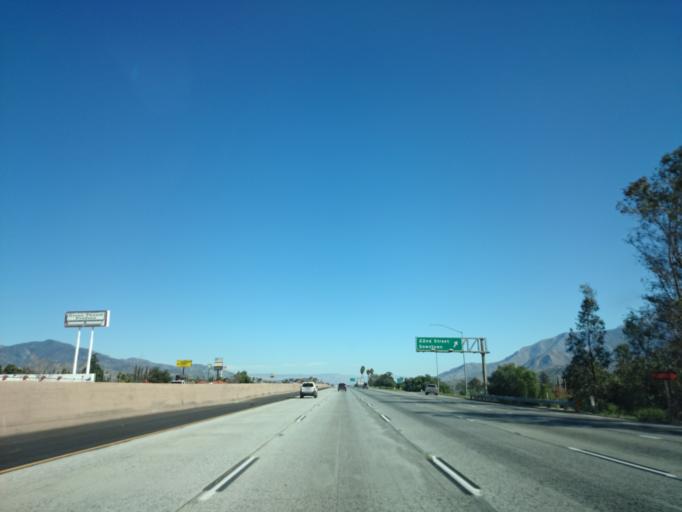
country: US
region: California
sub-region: Riverside County
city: Banning
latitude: 33.9242
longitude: -116.9058
